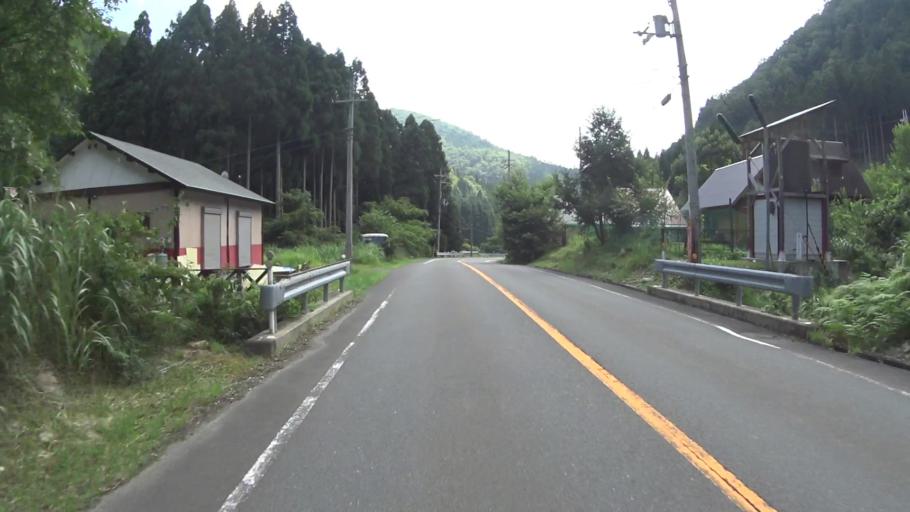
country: JP
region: Fukui
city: Obama
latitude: 35.3409
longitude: 135.5852
